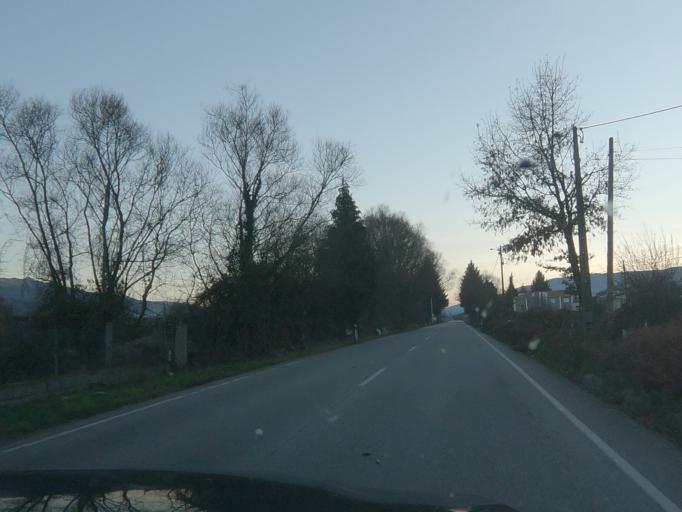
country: PT
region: Vila Real
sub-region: Vila Pouca de Aguiar
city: Vila Pouca de Aguiar
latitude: 41.4745
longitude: -7.6596
